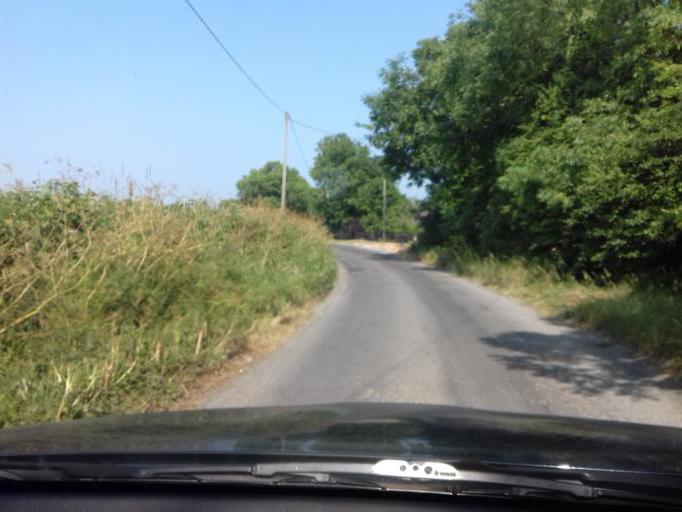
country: IE
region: Leinster
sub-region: An Mhi
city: Stamullin
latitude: 53.5973
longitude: -6.3161
